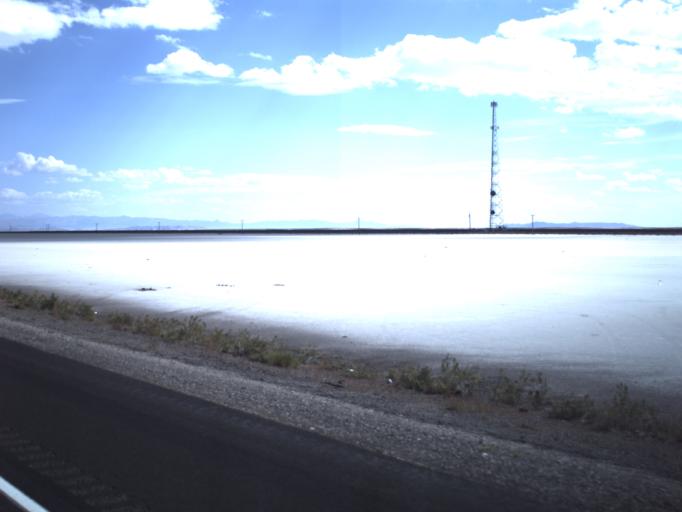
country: US
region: Utah
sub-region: Tooele County
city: Wendover
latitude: 40.7324
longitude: -113.5648
